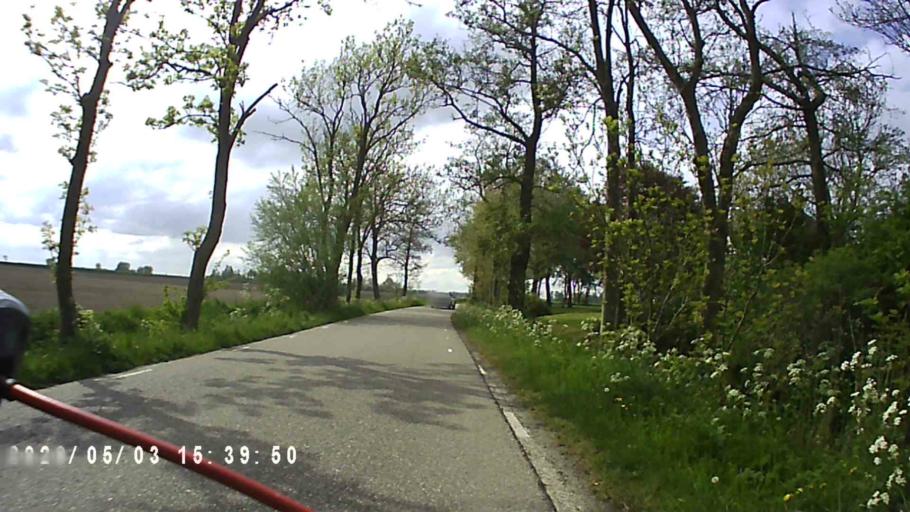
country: NL
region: Groningen
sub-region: Gemeente Zuidhorn
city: Oldehove
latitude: 53.3302
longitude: 6.4374
